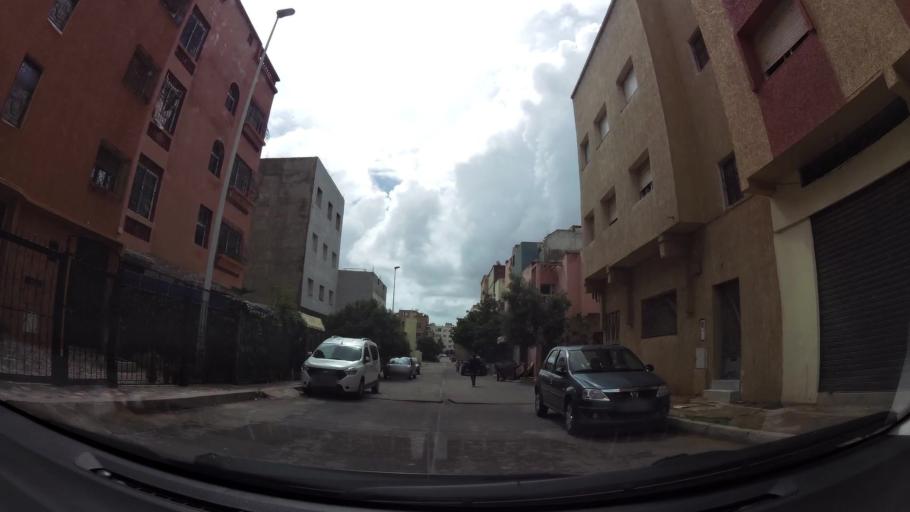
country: MA
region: Grand Casablanca
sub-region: Casablanca
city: Casablanca
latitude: 33.5662
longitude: -7.6973
